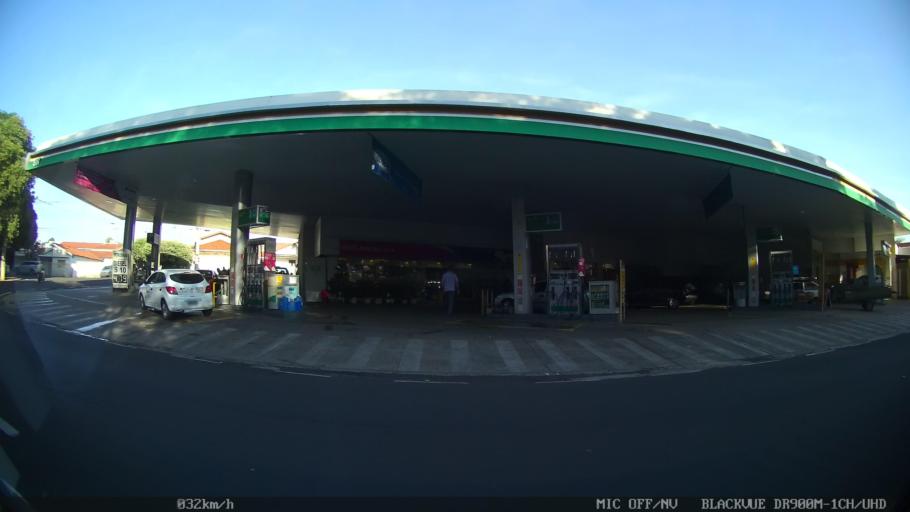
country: BR
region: Sao Paulo
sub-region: Sao Jose Do Rio Preto
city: Sao Jose do Rio Preto
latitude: -20.8202
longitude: -49.3661
